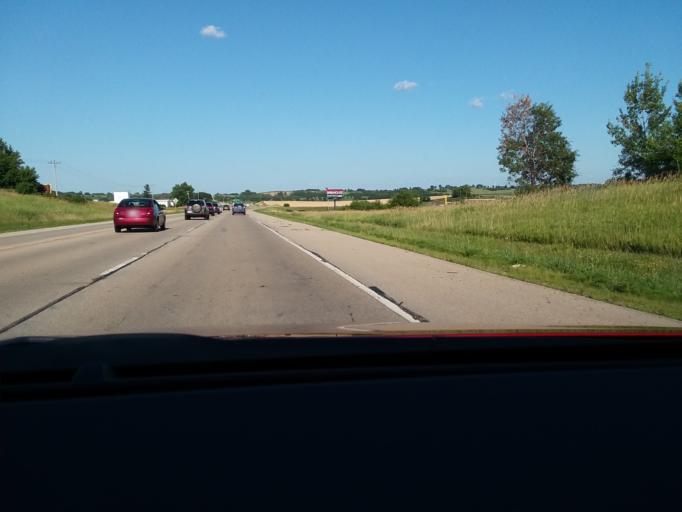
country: US
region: Wisconsin
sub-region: Dane County
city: Waunakee
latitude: 43.1918
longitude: -89.4284
